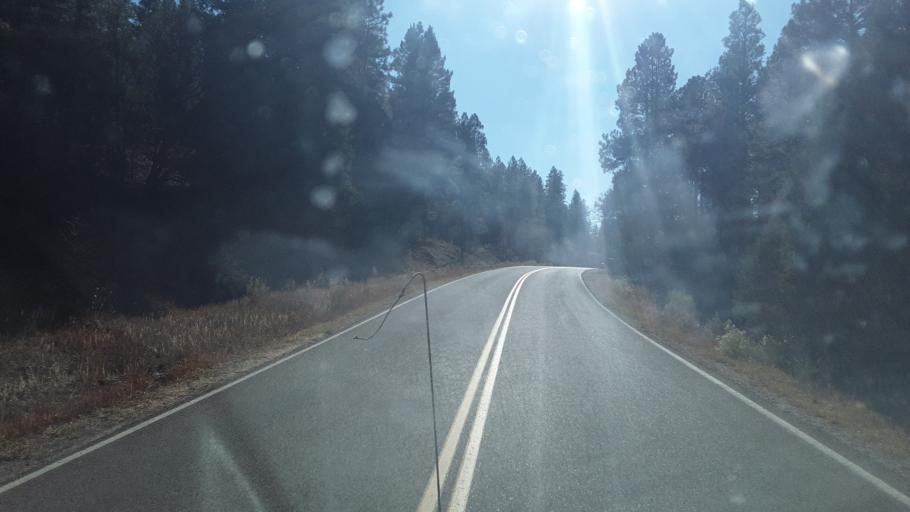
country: US
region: Colorado
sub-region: La Plata County
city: Durango
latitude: 37.4176
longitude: -107.8031
